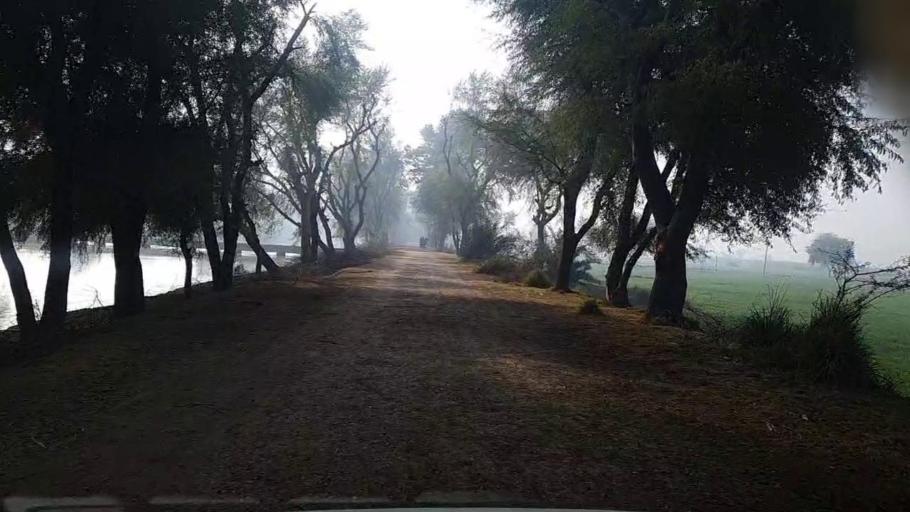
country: PK
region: Sindh
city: Khairpur
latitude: 27.9571
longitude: 69.6536
